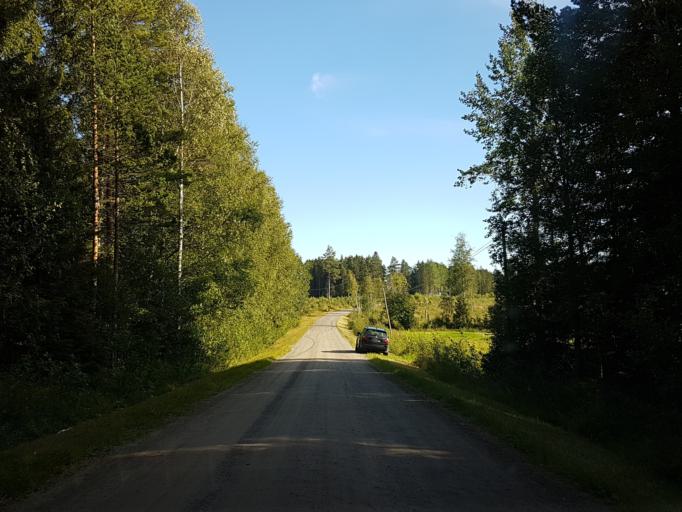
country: SE
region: Vaesterbotten
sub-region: Robertsfors Kommun
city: Robertsfors
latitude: 64.0581
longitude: 20.8685
